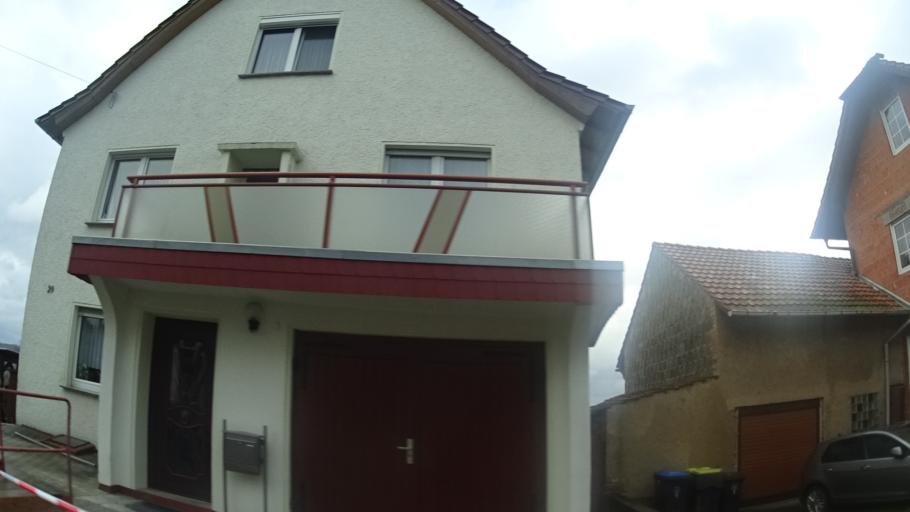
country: DE
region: Thuringia
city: Dankmarshausen
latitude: 50.9217
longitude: 10.0131
